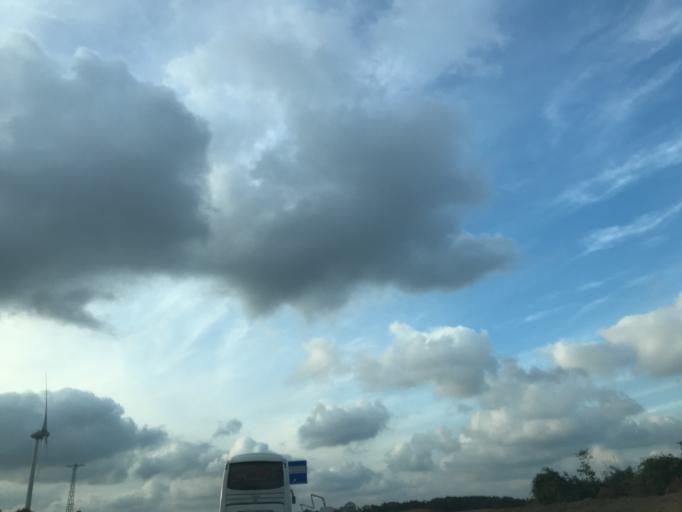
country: TR
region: Istanbul
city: Durusu
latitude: 41.2573
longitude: 28.6890
